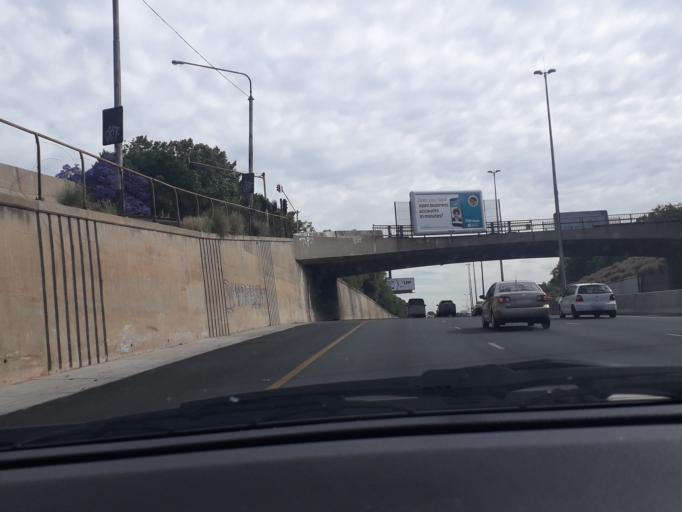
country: ZA
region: Gauteng
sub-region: City of Johannesburg Metropolitan Municipality
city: Johannesburg
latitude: -26.1781
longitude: 28.0370
